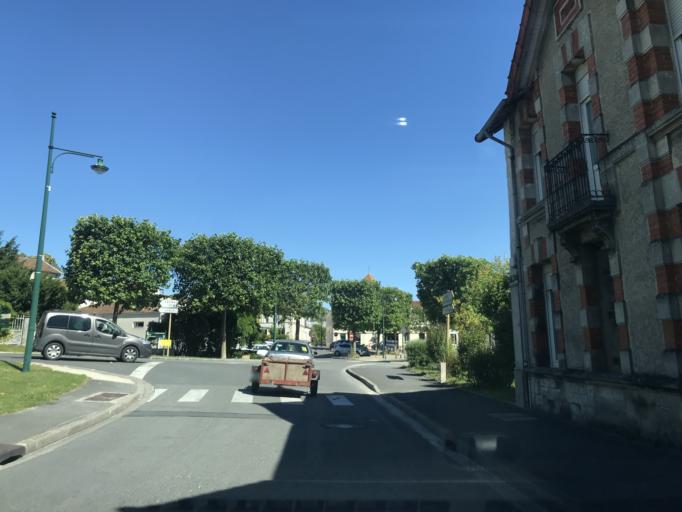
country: FR
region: Poitou-Charentes
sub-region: Departement de la Charente
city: Barbezieux-Saint-Hilaire
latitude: 45.4703
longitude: -0.1524
